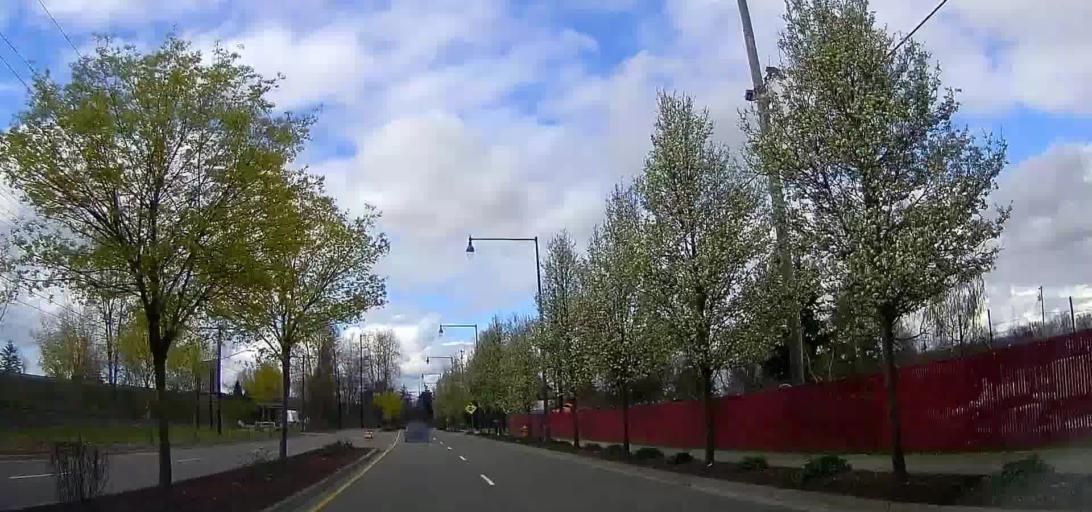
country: US
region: Washington
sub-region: Snohomish County
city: Smokey Point
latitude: 48.1222
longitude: -122.1833
